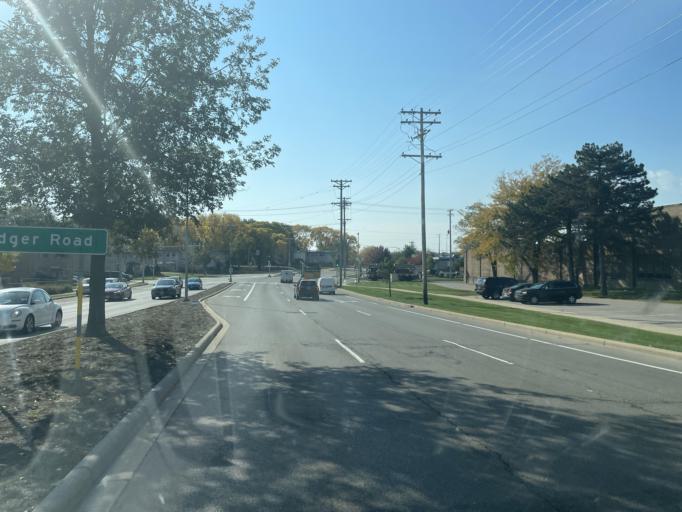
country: US
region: Wisconsin
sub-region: Dane County
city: Madison
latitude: 43.0396
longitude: -89.4040
